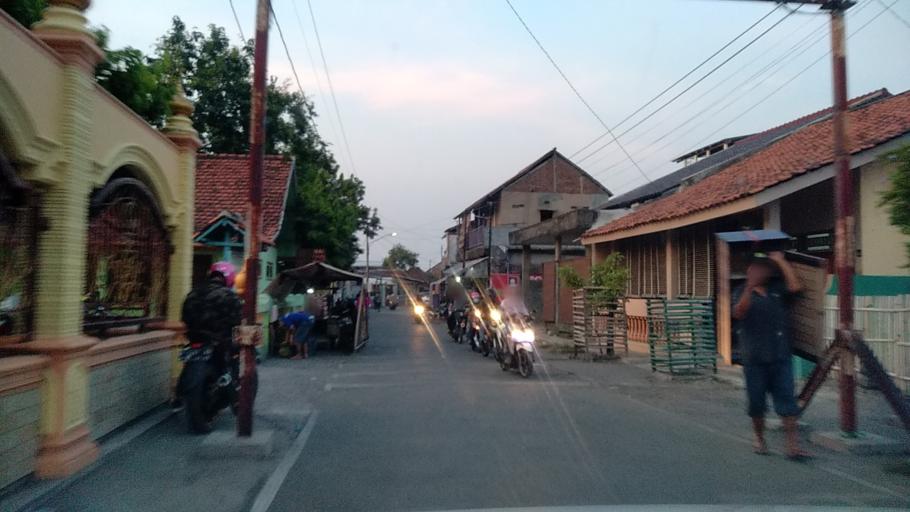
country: ID
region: Central Java
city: Semarang
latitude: -6.9758
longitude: 110.3316
